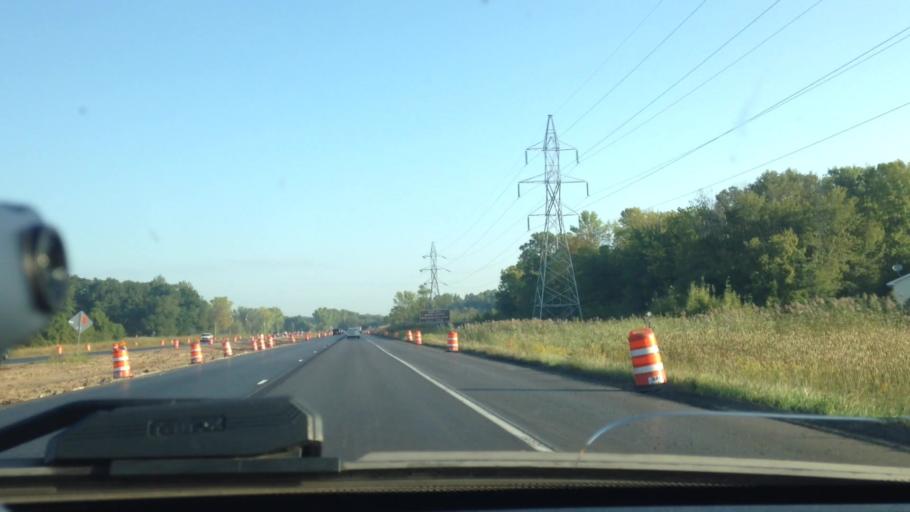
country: US
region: Wisconsin
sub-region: Brown County
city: Suamico
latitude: 44.6204
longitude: -88.0497
